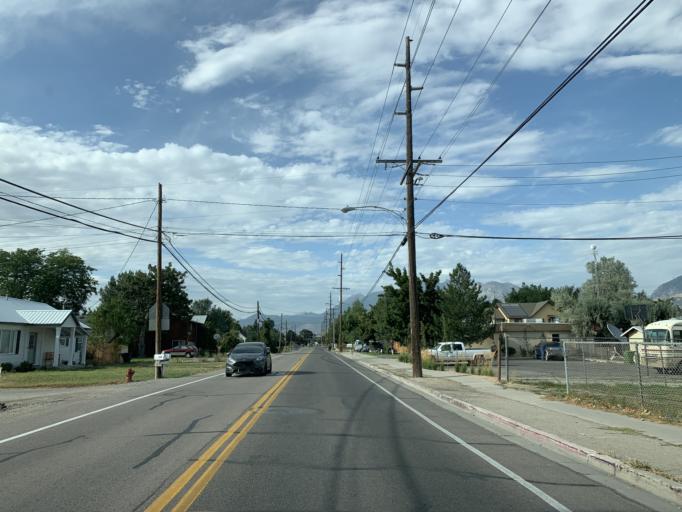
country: US
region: Utah
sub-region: Utah County
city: Provo
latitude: 40.2295
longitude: -111.6874
